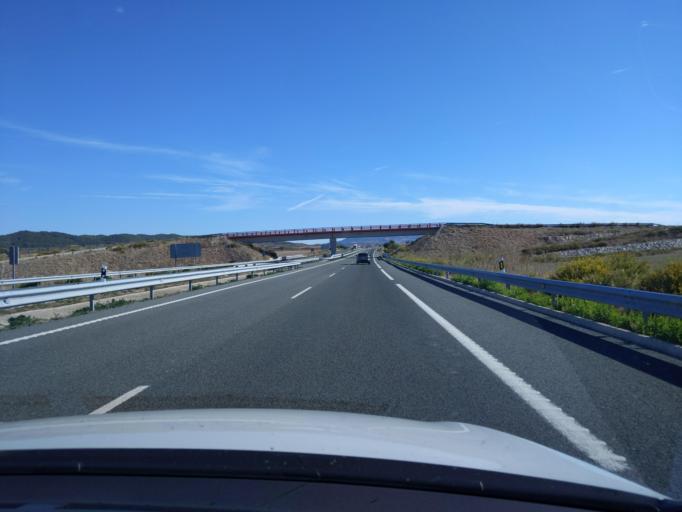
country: ES
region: Navarre
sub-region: Provincia de Navarra
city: Los Arcos
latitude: 42.5628
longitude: -2.1771
